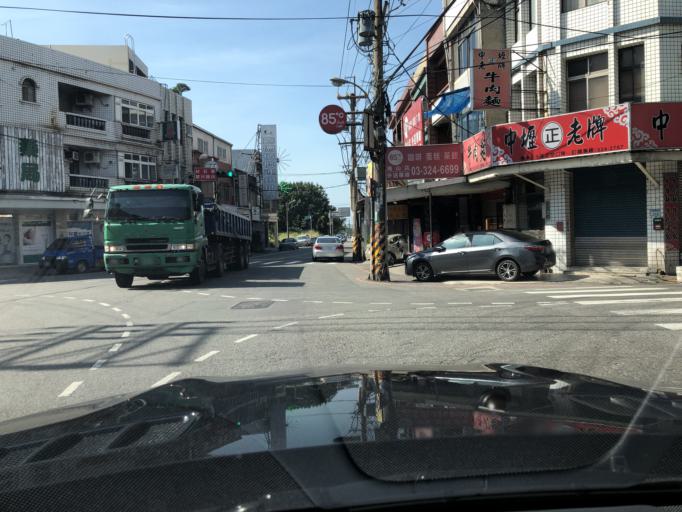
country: TW
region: Taiwan
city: Taoyuan City
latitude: 25.0855
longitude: 121.2866
